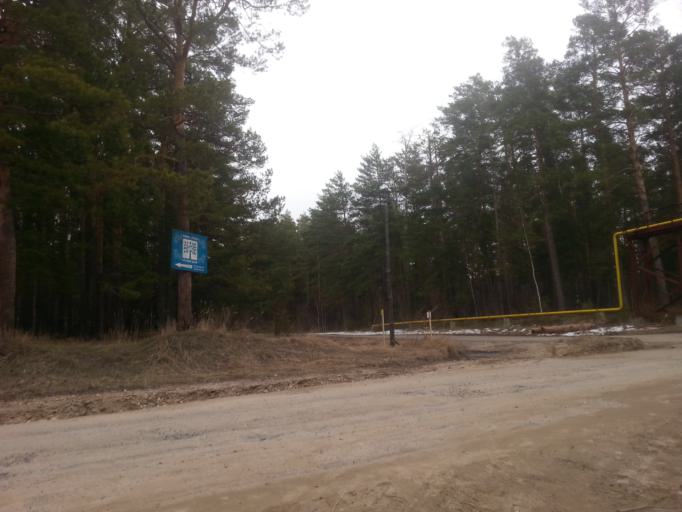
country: RU
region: Altai Krai
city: Yuzhnyy
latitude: 53.2793
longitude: 83.7355
